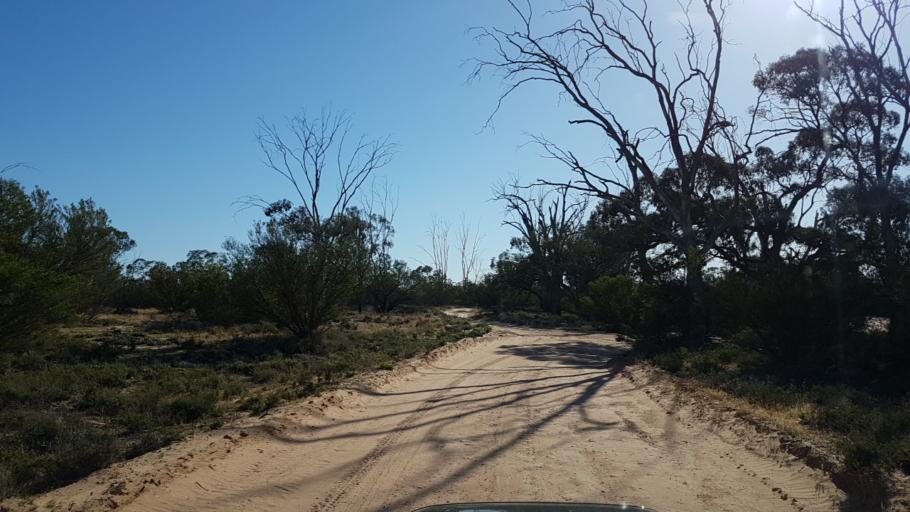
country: AU
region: South Australia
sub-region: Loxton Waikerie
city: Waikerie
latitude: -34.1581
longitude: 140.0265
